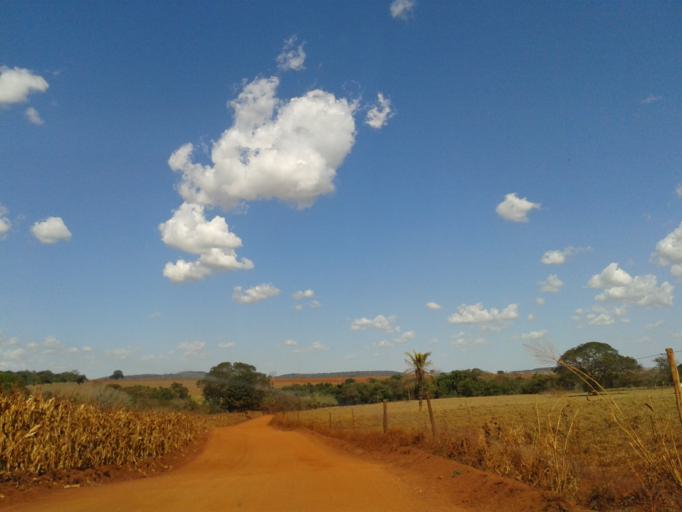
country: BR
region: Minas Gerais
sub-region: Capinopolis
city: Capinopolis
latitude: -18.6060
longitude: -49.4952
